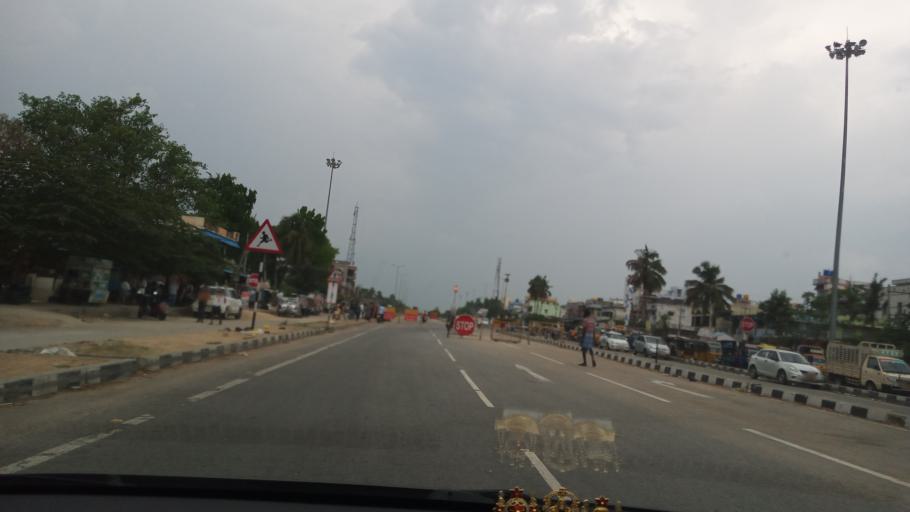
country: IN
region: Karnataka
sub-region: Kolar
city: Mulbagal
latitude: 13.1985
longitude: 78.5157
